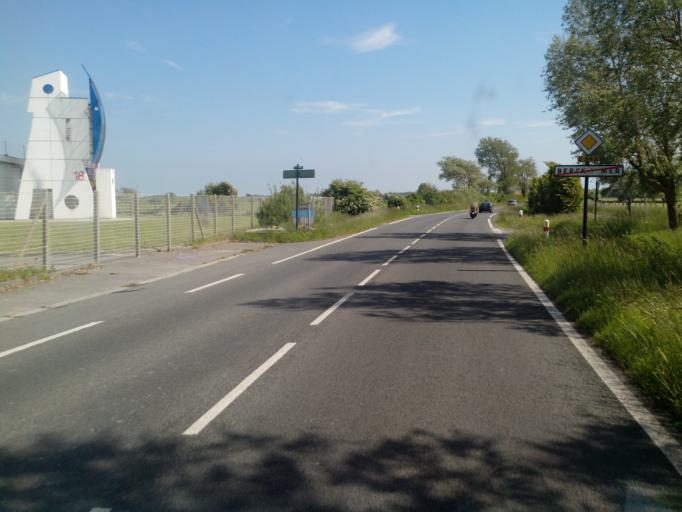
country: FR
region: Nord-Pas-de-Calais
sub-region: Departement du Pas-de-Calais
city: Berck
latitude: 50.3983
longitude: 1.5996
